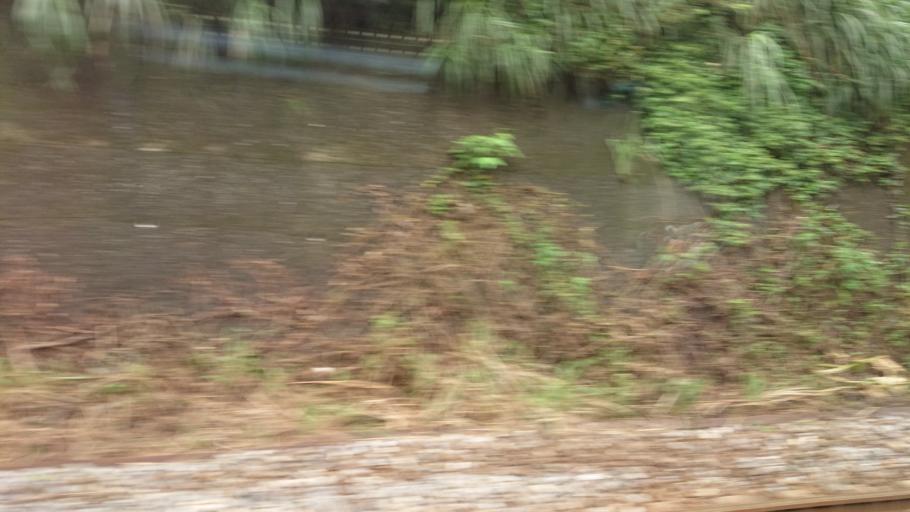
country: TW
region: Taiwan
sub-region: Keelung
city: Keelung
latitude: 25.0984
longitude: 121.8327
